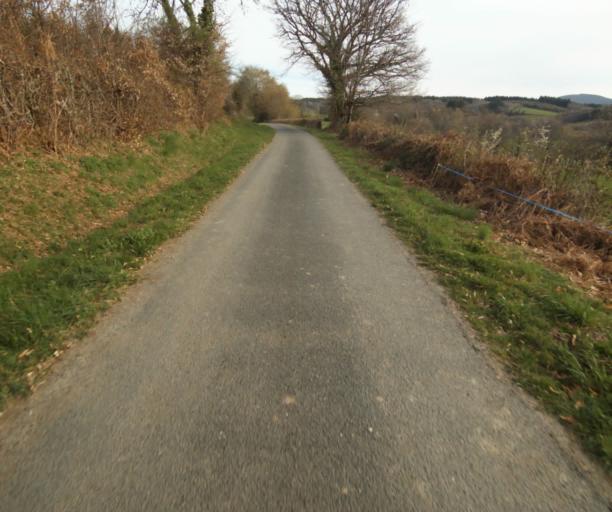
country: FR
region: Limousin
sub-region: Departement de la Correze
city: Chamboulive
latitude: 45.4389
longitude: 1.7879
